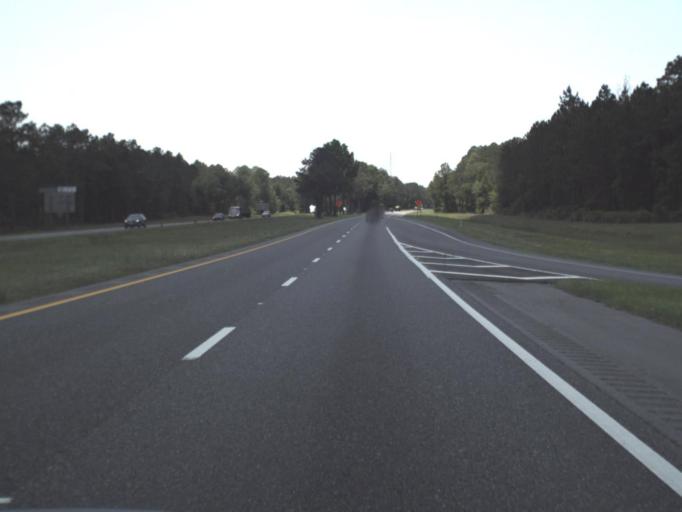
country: US
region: Florida
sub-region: Columbia County
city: Five Points
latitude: 30.2419
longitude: -82.6416
